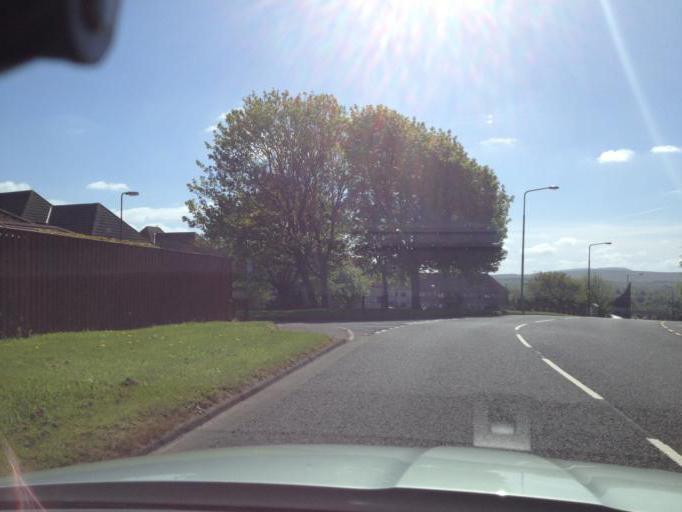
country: GB
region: Scotland
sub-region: West Lothian
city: Livingston
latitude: 55.8975
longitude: -3.5037
